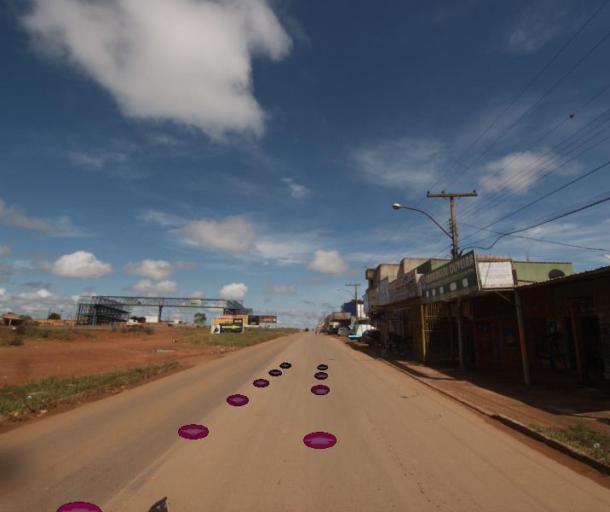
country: BR
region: Federal District
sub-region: Brasilia
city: Brasilia
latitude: -15.7363
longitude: -48.2876
